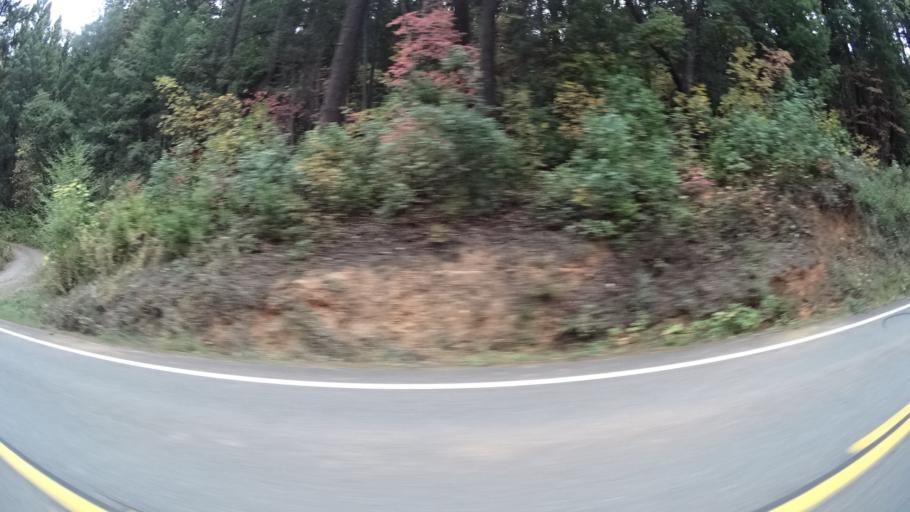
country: US
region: California
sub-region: Siskiyou County
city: Happy Camp
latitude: 41.8007
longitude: -123.3442
